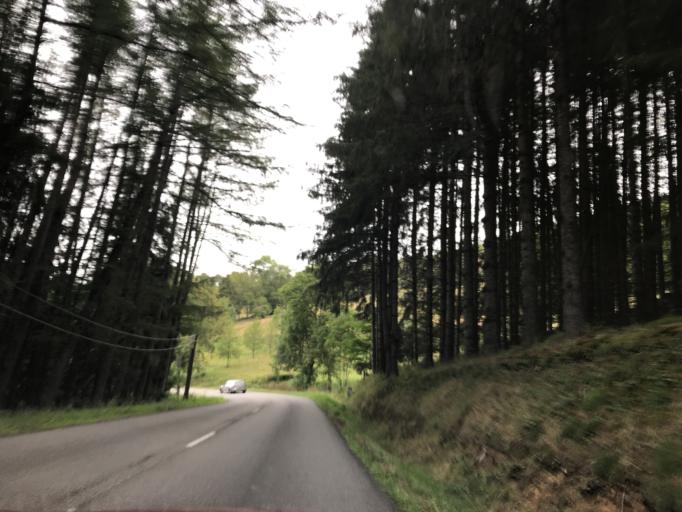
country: FR
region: Rhone-Alpes
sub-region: Departement de la Loire
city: Sail-sous-Couzan
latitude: 45.7003
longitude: 3.8677
